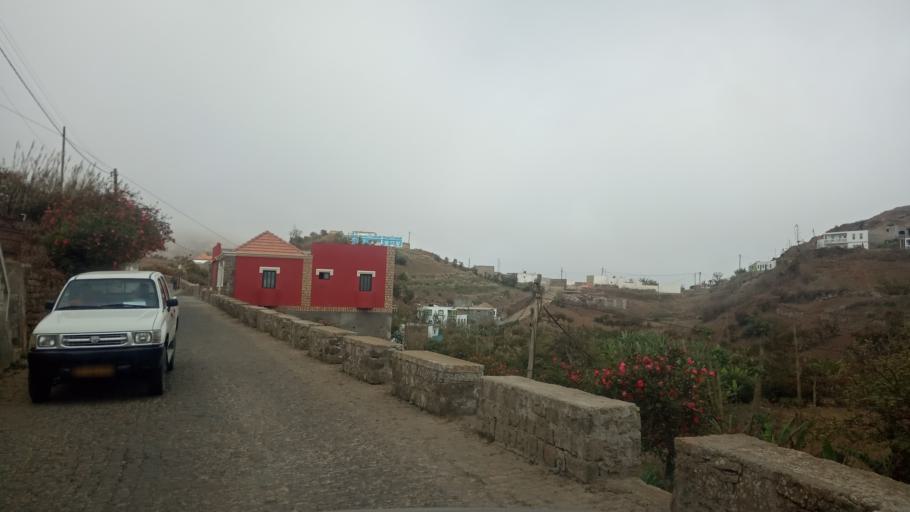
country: CV
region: Brava
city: Vila Nova Sintra
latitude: 14.8714
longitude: -24.7039
